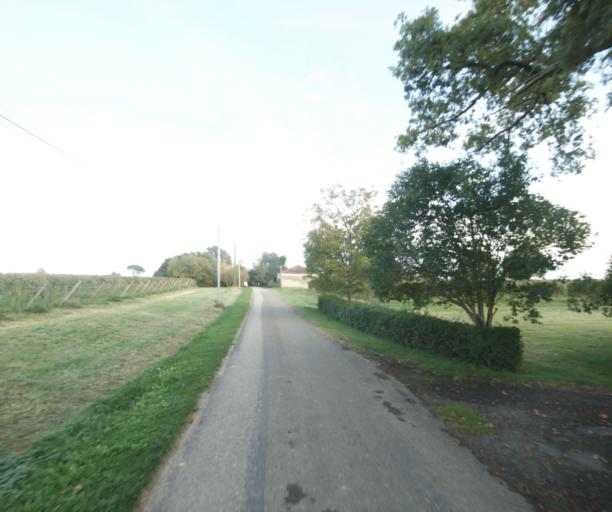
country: FR
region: Midi-Pyrenees
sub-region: Departement du Gers
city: Le Houga
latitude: 43.8545
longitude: -0.1411
